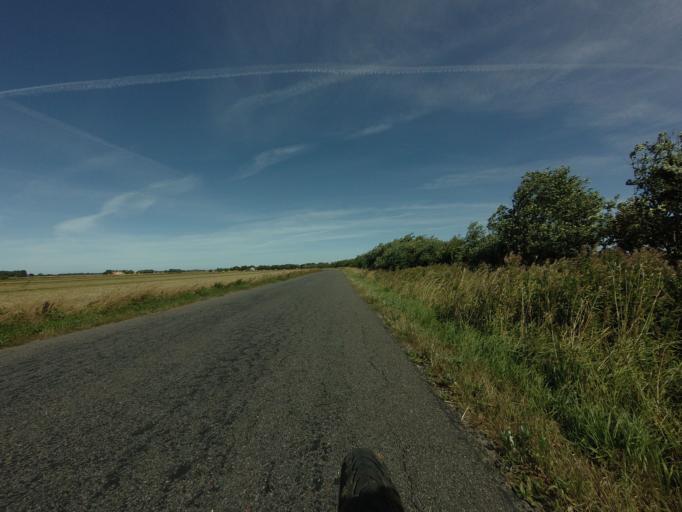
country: DK
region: North Denmark
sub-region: Bronderslev Kommune
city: Bronderslev
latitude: 57.3122
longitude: 9.8116
